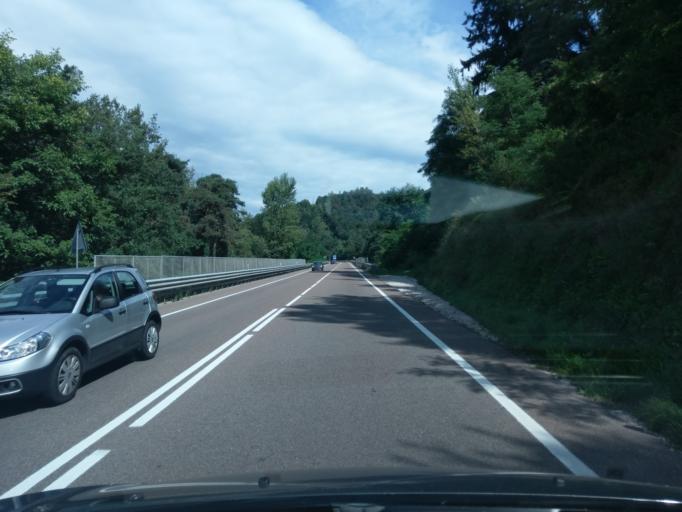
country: IT
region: Trentino-Alto Adige
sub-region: Provincia di Trento
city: Denno
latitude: 46.2743
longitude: 11.0645
